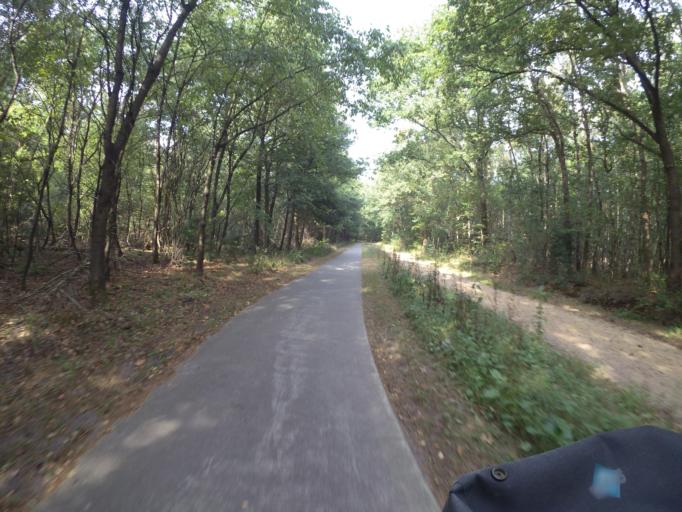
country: NL
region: Drenthe
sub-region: Gemeente Westerveld
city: Dwingeloo
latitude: 52.9004
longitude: 6.3648
